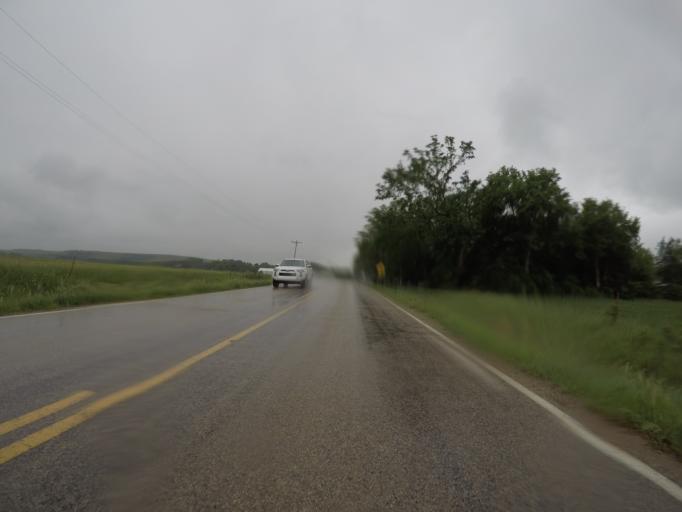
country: US
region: Kansas
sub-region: Pottawatomie County
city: Westmoreland
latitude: 39.4008
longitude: -96.1839
